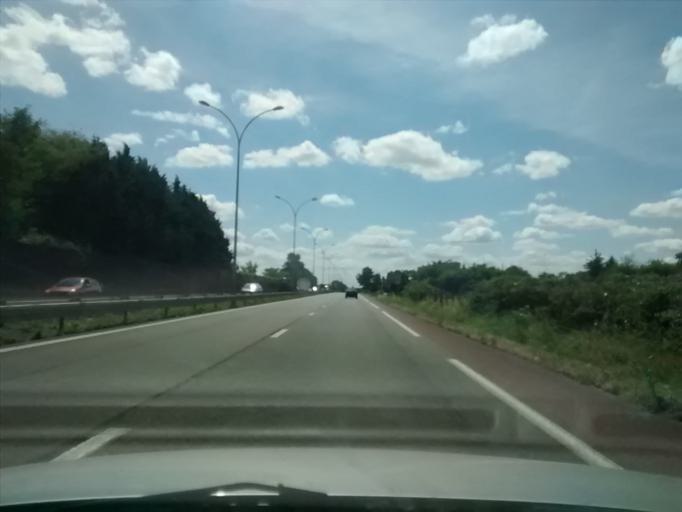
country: FR
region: Pays de la Loire
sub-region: Departement de la Sarthe
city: Le Mans
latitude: 48.0074
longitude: 0.1719
